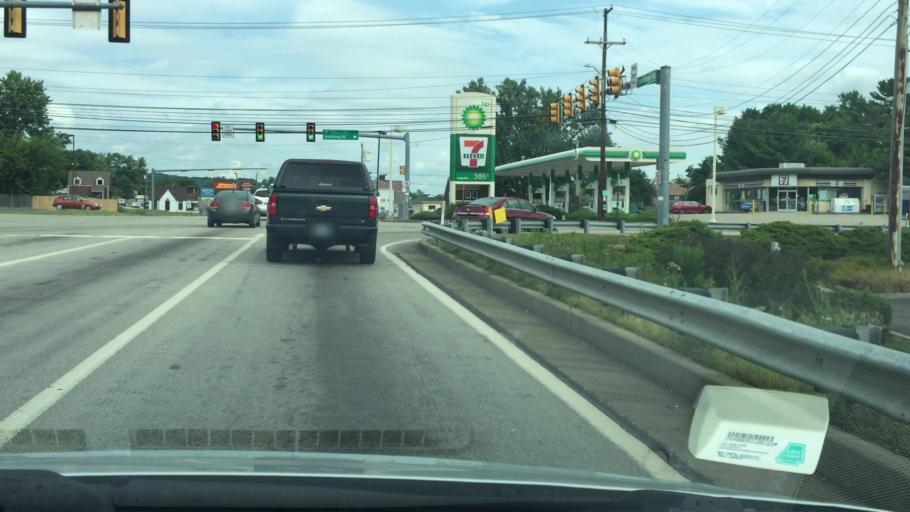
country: US
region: Pennsylvania
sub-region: Allegheny County
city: Tarentum
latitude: 40.5866
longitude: -79.7492
